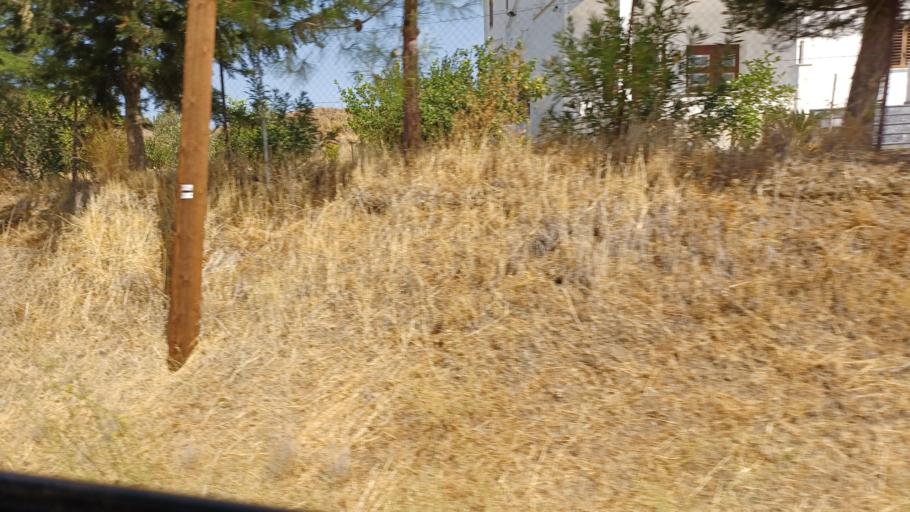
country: CY
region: Lefkosia
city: Lefka
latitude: 35.0663
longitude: 32.8946
